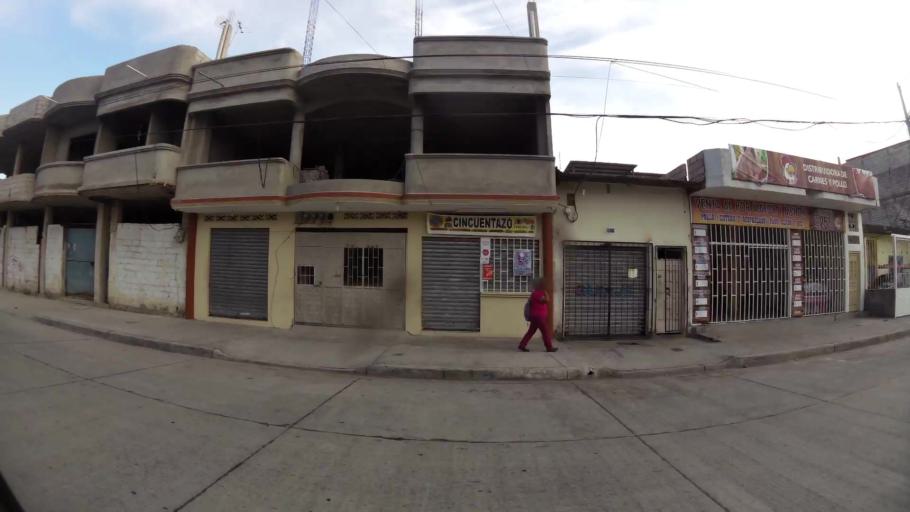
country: EC
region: Guayas
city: Eloy Alfaro
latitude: -2.0881
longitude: -79.9030
